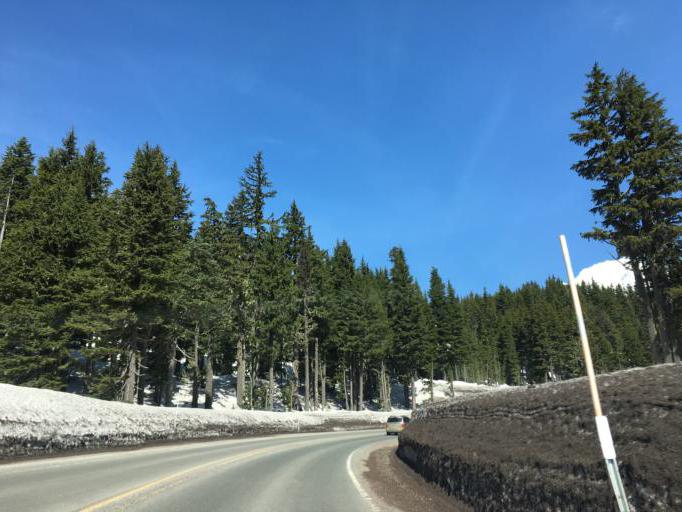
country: US
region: Oregon
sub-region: Clackamas County
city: Mount Hood Village
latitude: 45.3197
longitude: -121.7101
